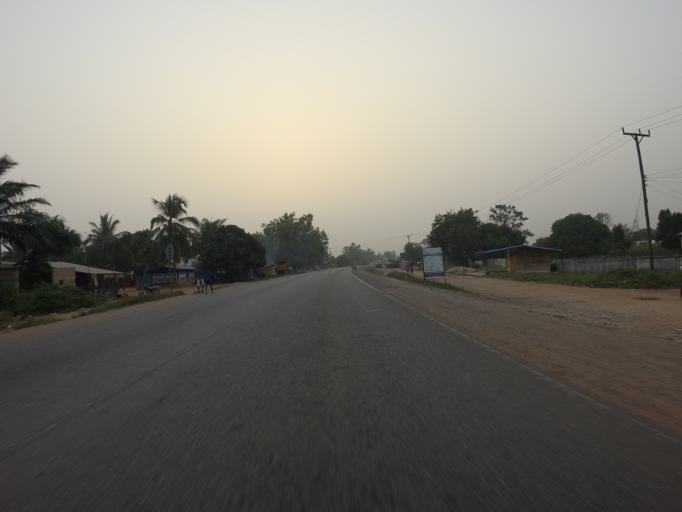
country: GH
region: Volta
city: Anloga
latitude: 5.9912
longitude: 0.5782
